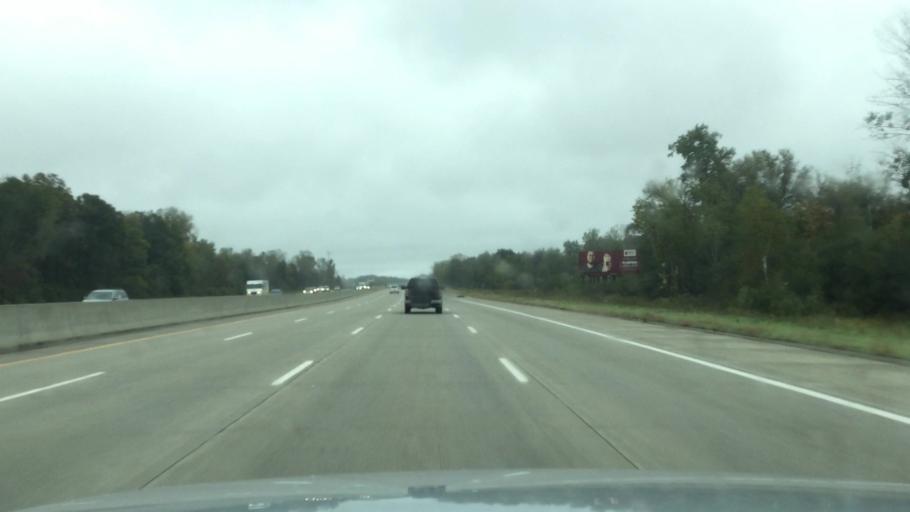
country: US
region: Michigan
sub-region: Saginaw County
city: Birch Run
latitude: 43.3062
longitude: -83.8347
